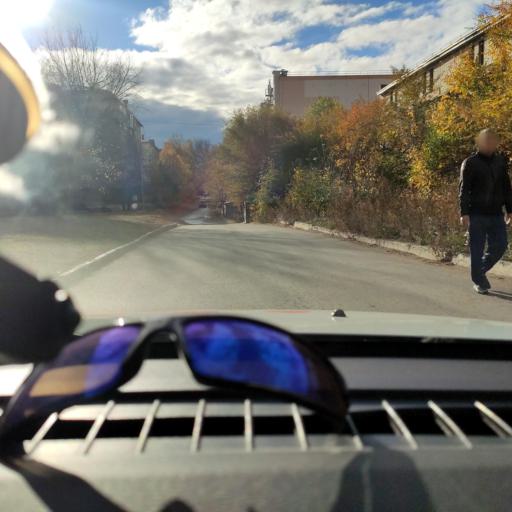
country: RU
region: Samara
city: Samara
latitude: 53.2153
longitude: 50.1725
